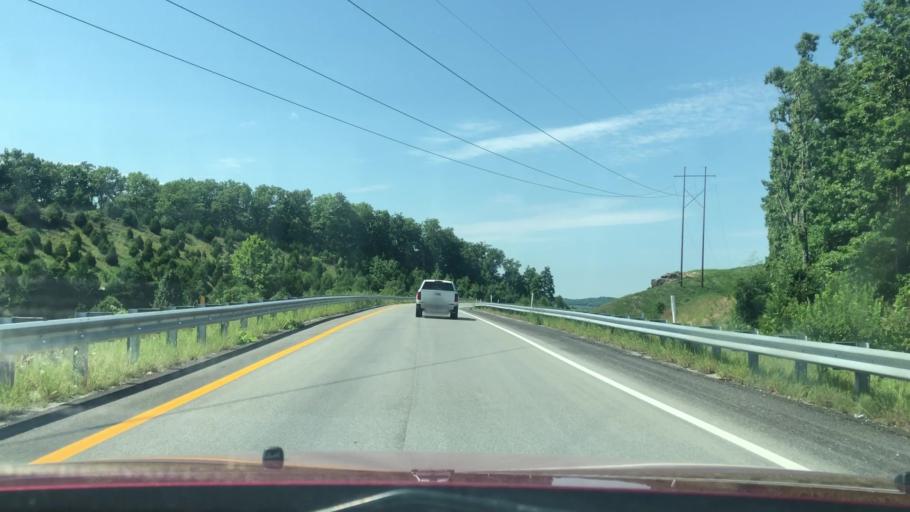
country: US
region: Missouri
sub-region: Taney County
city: Branson
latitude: 36.6772
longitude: -93.3157
